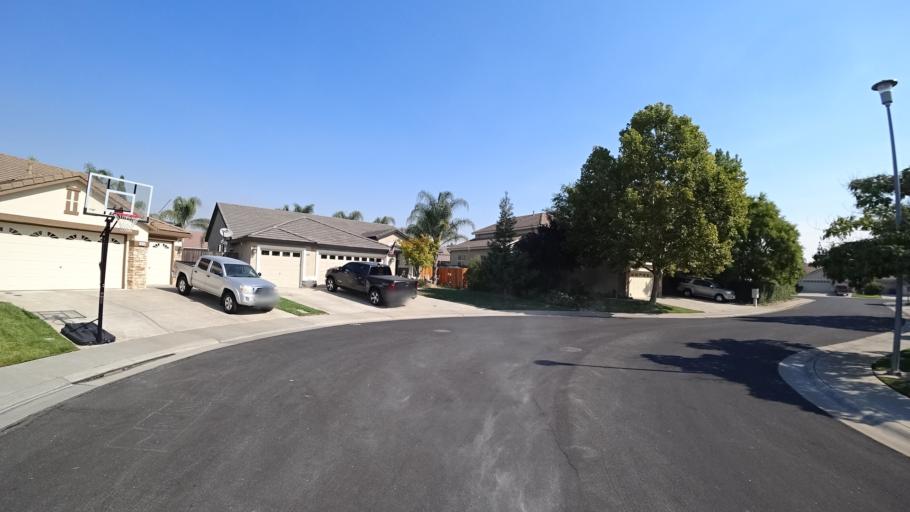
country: US
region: California
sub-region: Sacramento County
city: Laguna
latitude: 38.3845
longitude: -121.4346
